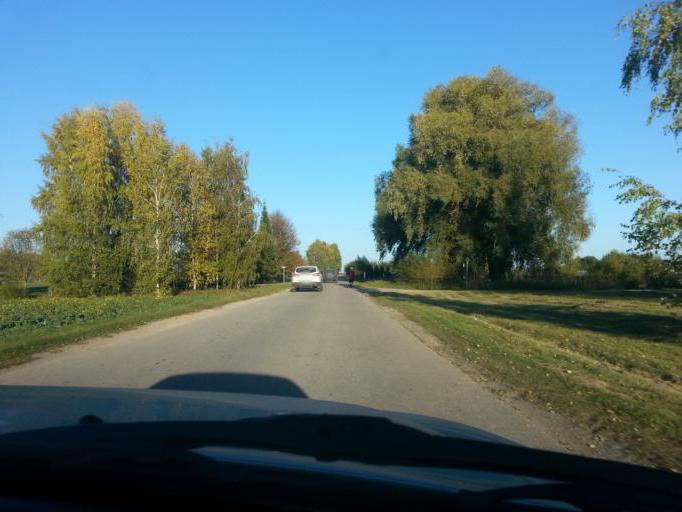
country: LV
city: Tervete
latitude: 56.6180
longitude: 23.4566
